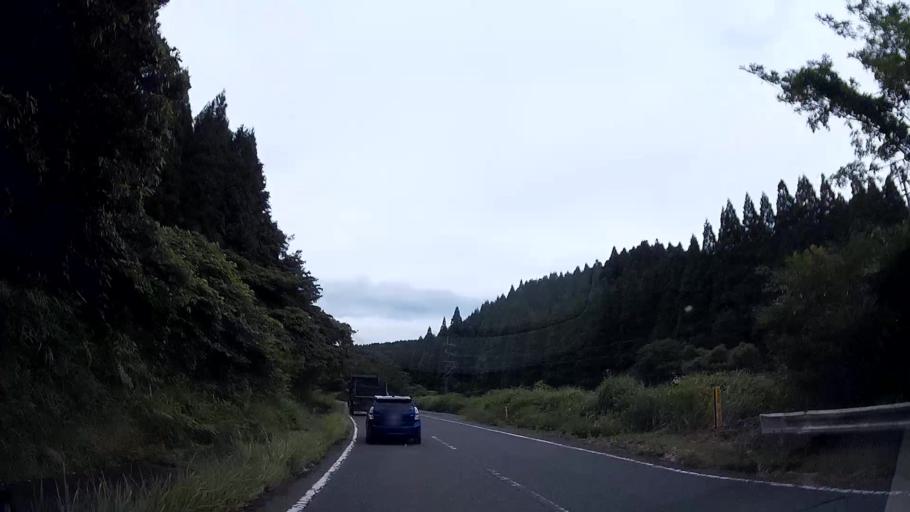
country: JP
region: Kumamoto
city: Aso
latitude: 33.1231
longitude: 131.0109
